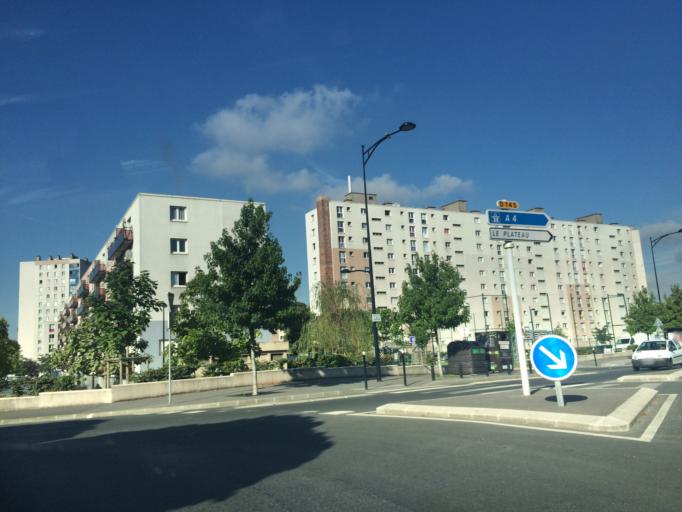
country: FR
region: Ile-de-France
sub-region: Departement du Val-de-Marne
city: Chennevieres-sur-Marne
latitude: 48.8099
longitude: 2.5431
